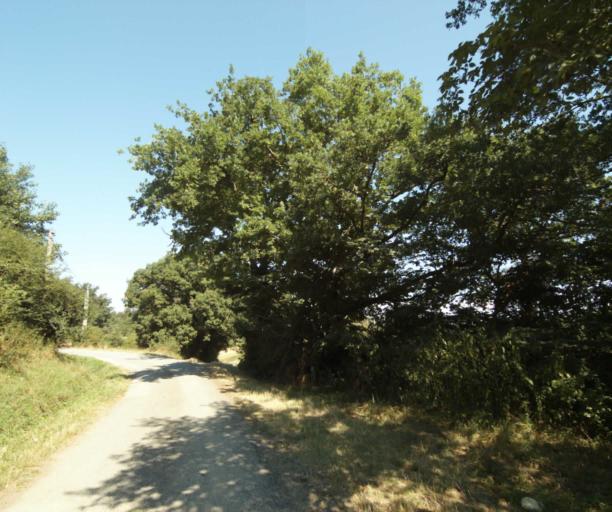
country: FR
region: Midi-Pyrenees
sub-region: Departement de l'Ariege
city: Lezat-sur-Leze
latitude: 43.2936
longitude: 1.3329
